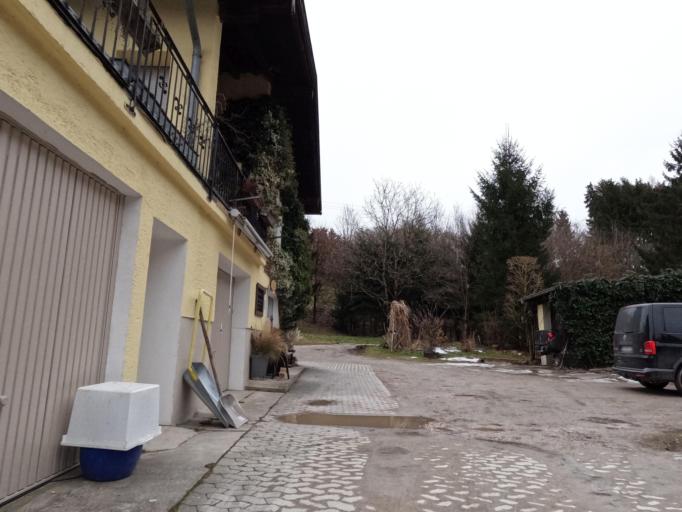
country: DE
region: Bavaria
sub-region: Upper Bavaria
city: Vachendorf
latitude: 47.8494
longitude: 12.5965
